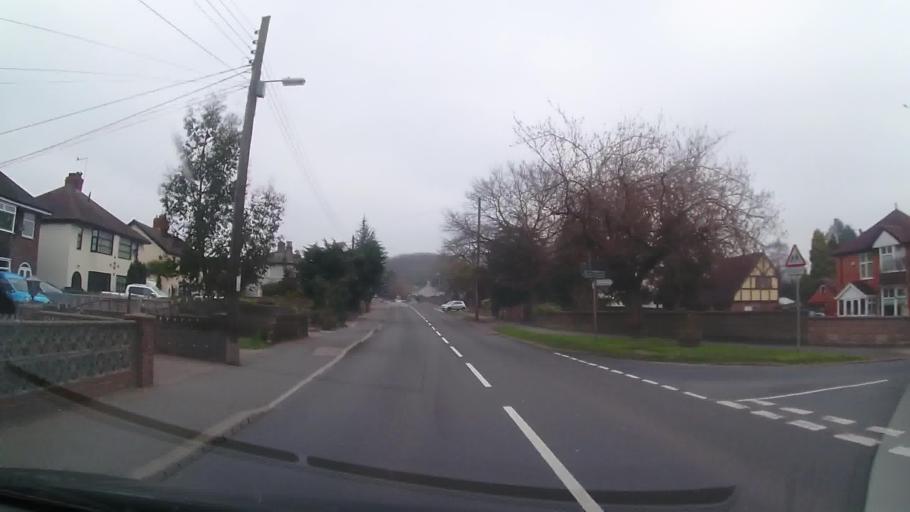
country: GB
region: England
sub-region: Staffordshire
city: Standon
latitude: 52.9596
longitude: -2.3066
